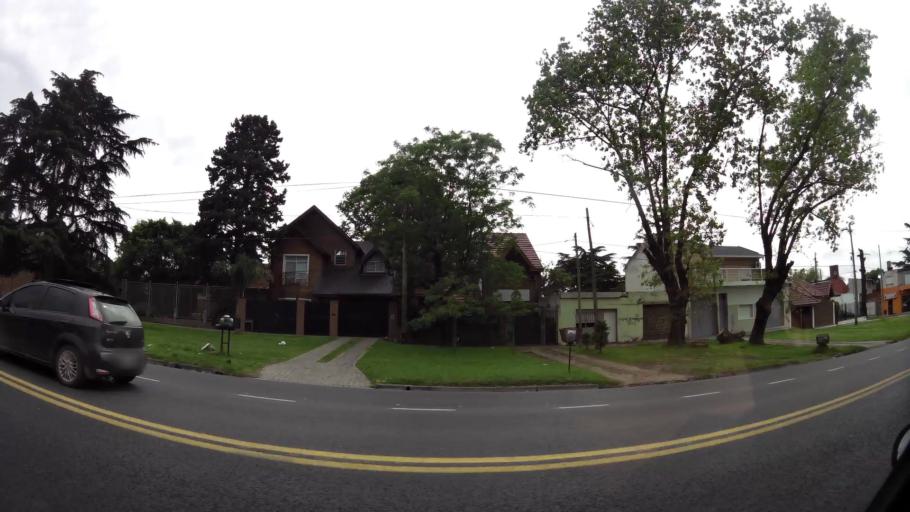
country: AR
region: Buenos Aires
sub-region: Partido de Quilmes
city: Quilmes
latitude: -34.7633
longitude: -58.2857
